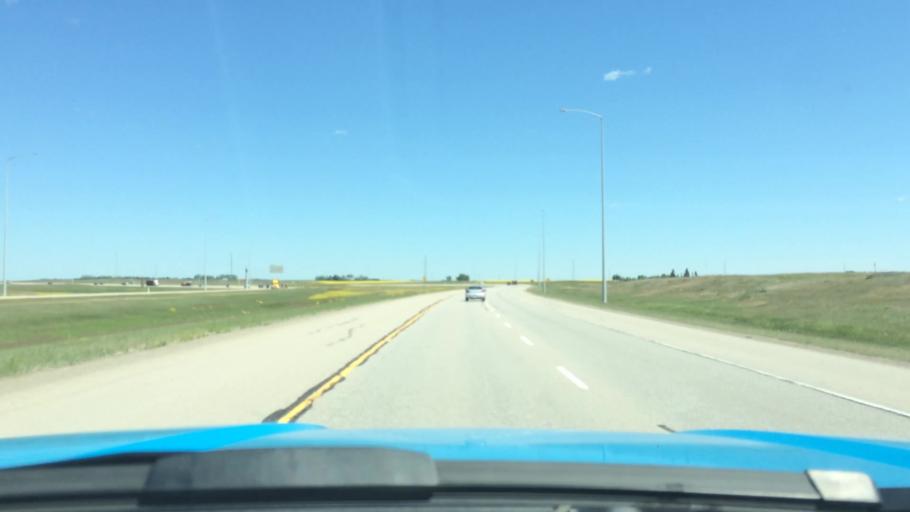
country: CA
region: Alberta
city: Chestermere
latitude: 51.1663
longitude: -113.9173
